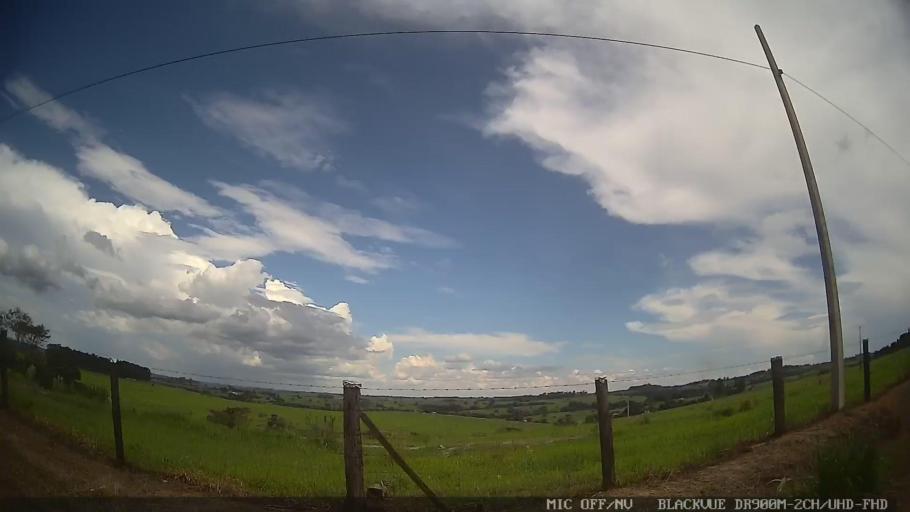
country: BR
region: Sao Paulo
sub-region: Conchas
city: Conchas
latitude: -22.9508
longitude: -47.9831
